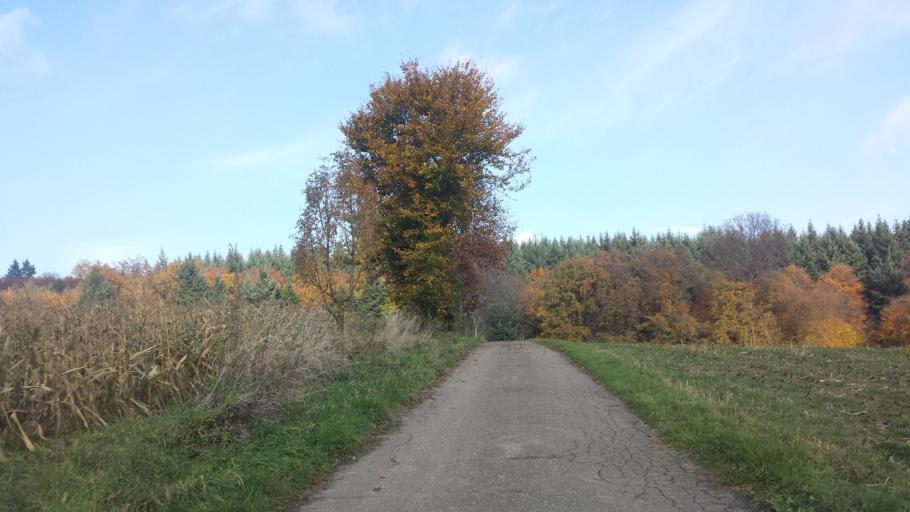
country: DE
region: Baden-Wuerttemberg
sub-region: Karlsruhe Region
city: Gondelsheim
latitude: 49.1034
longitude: 8.6716
